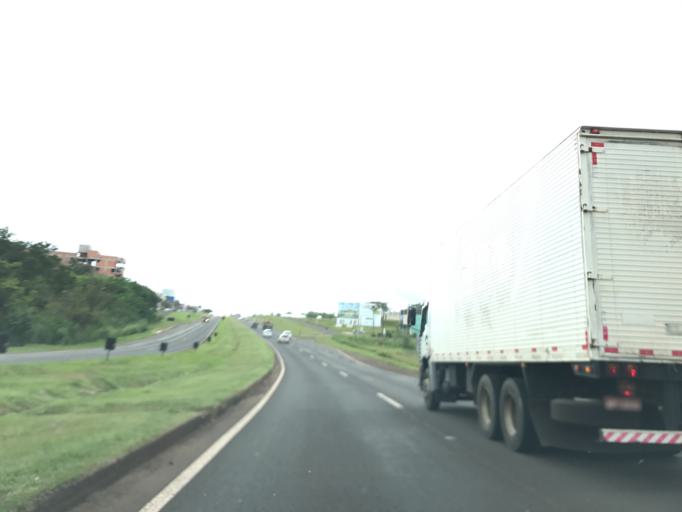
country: BR
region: Parana
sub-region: Cambe
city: Cambe
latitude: -23.2960
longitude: -51.2717
